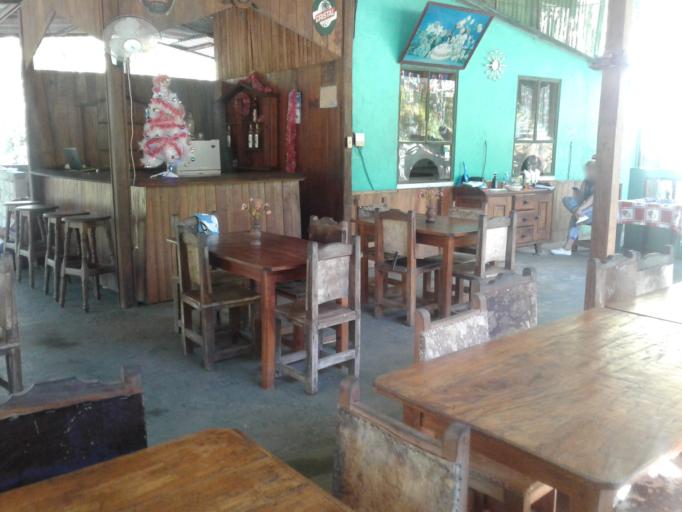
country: CU
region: Granma
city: Bartolome Maso
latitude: 20.0424
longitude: -76.9033
